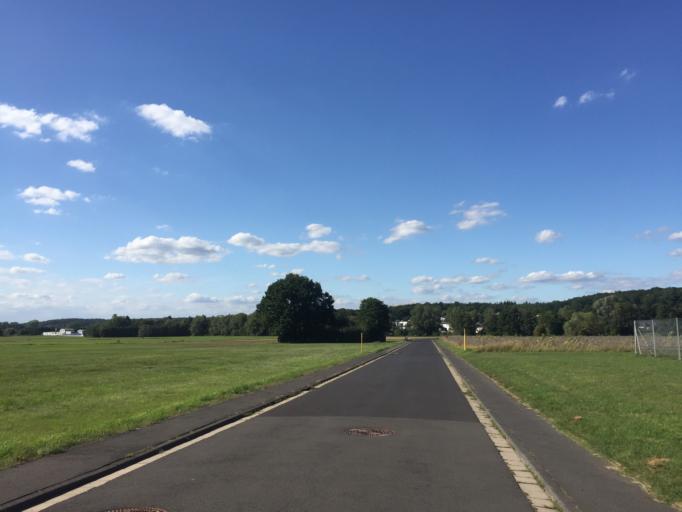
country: DE
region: Hesse
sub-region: Regierungsbezirk Giessen
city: Langgons
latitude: 50.5327
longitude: 8.6840
